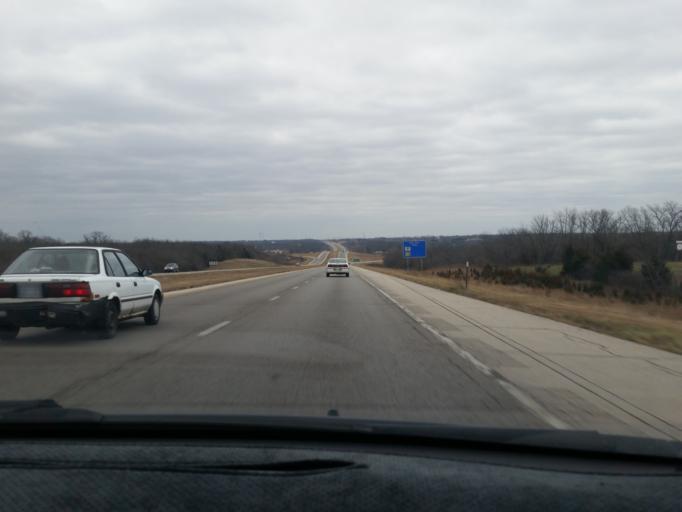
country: US
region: Kansas
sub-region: Johnson County
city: De Soto
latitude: 38.9612
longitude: -94.9987
